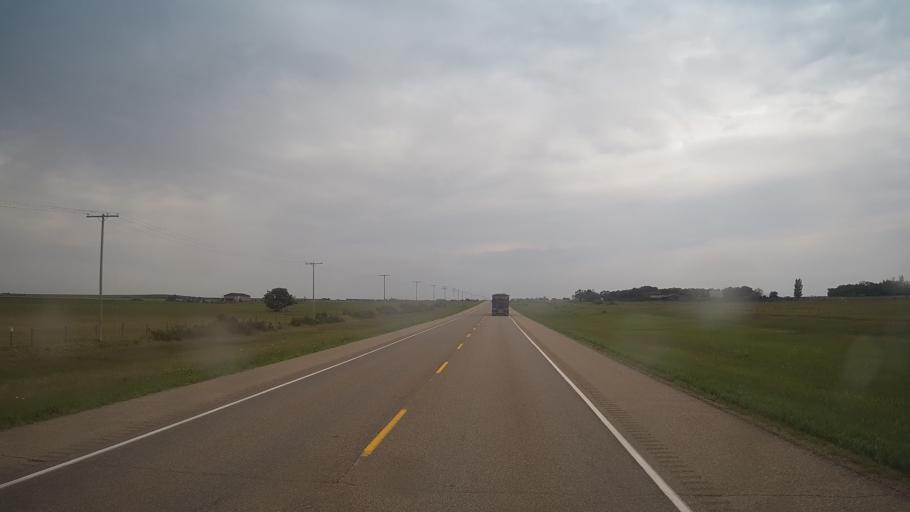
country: CA
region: Saskatchewan
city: Langham
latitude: 52.1288
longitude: -107.1606
